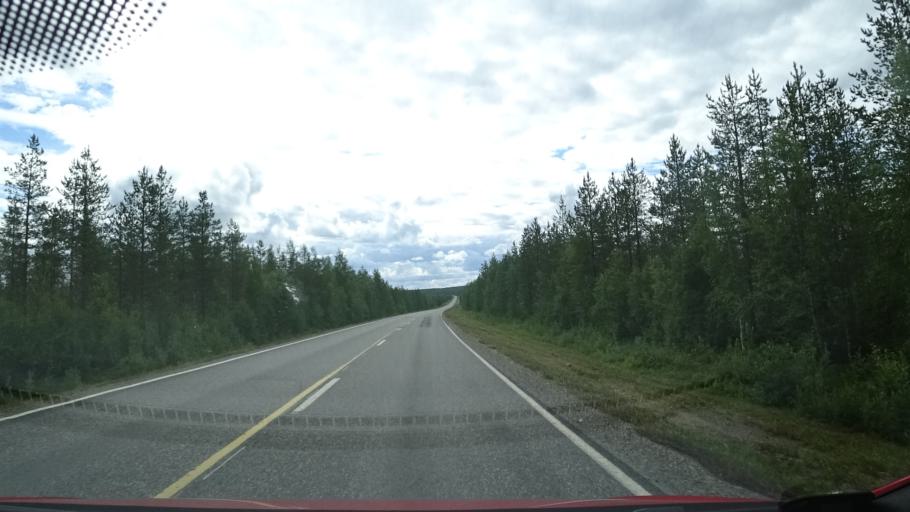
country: FI
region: Lapland
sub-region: Tunturi-Lappi
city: Kittilae
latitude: 67.5517
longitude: 24.9207
